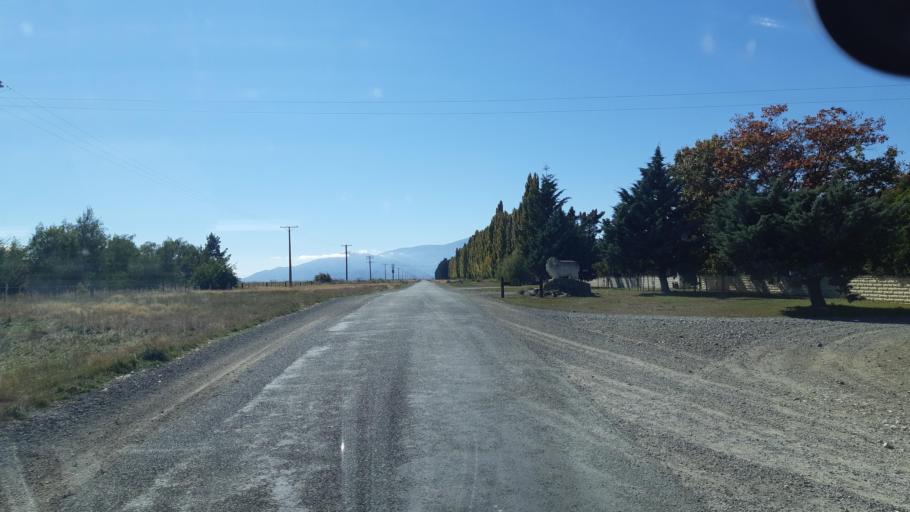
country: NZ
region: Otago
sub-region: Queenstown-Lakes District
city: Wanaka
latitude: -44.5361
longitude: 169.8716
